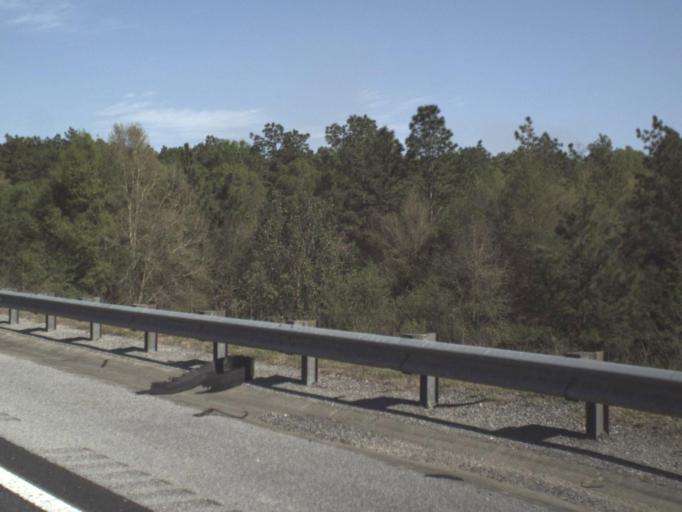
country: US
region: Florida
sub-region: Okaloosa County
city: Crestview
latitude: 30.7133
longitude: -86.6962
